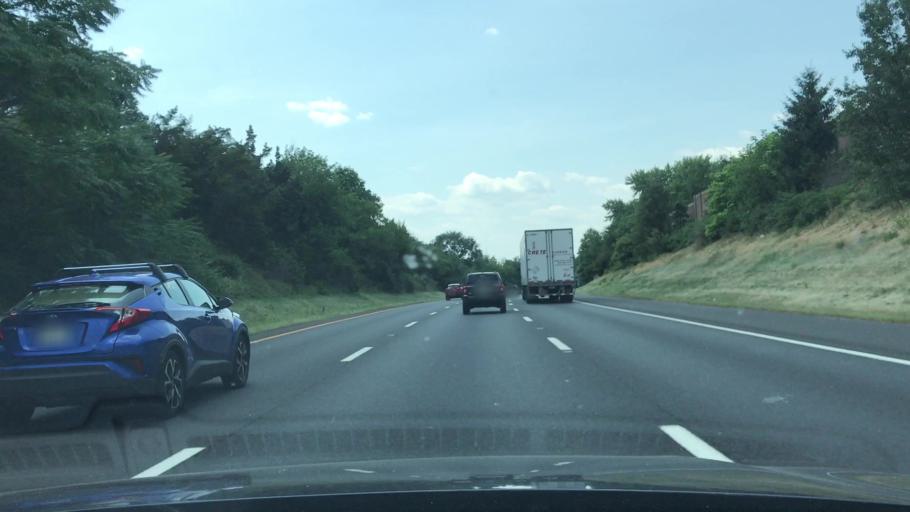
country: US
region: New Jersey
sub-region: Somerset County
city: Somerville
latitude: 40.5846
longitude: -74.6096
